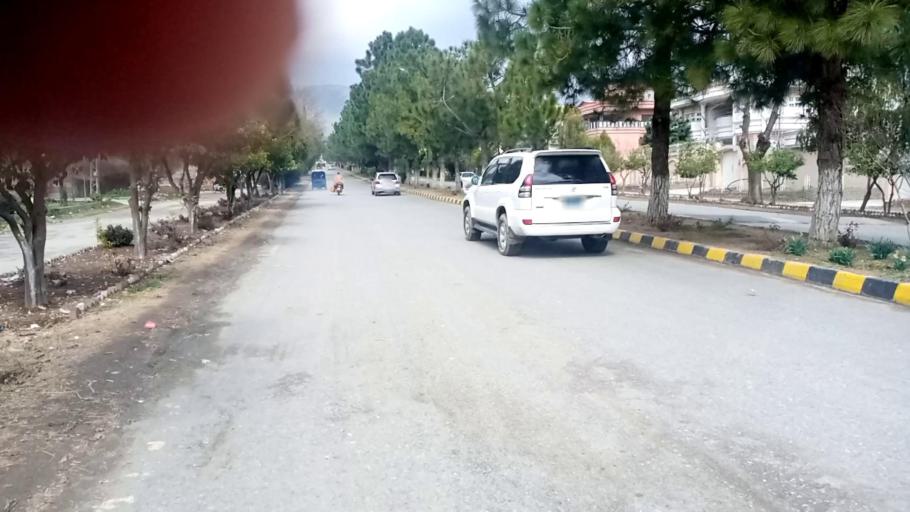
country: PK
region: Khyber Pakhtunkhwa
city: Mingora
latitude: 34.8207
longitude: 72.3405
